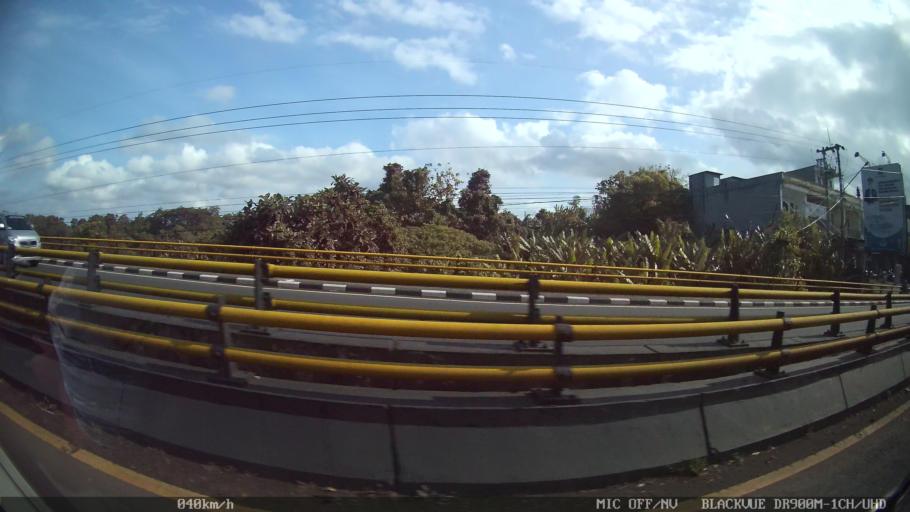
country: ID
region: Bali
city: Banjar Bongangede
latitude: -8.5510
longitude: 115.1263
